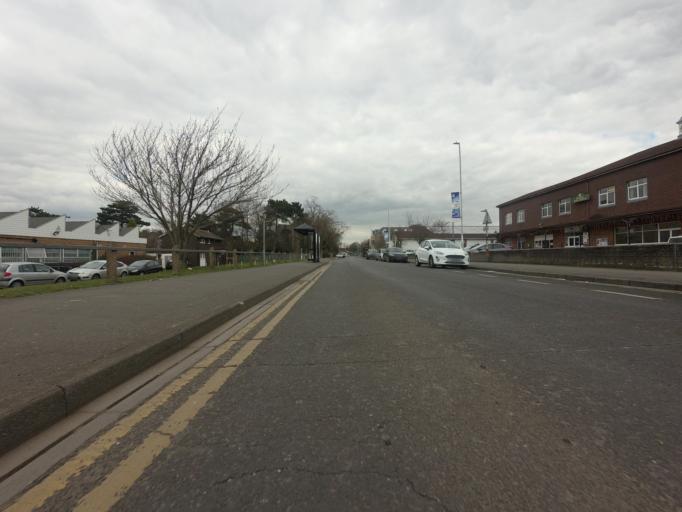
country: GB
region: England
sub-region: Kent
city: Swanley
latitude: 51.3963
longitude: 0.1707
